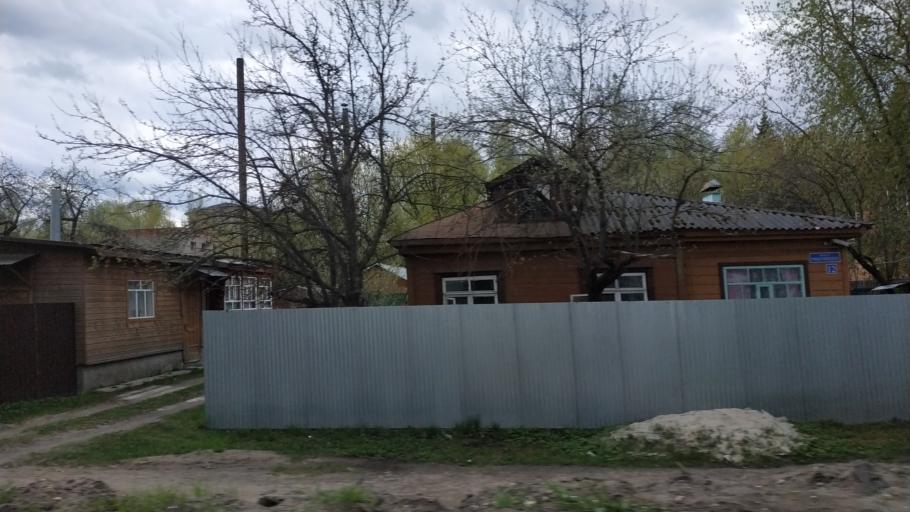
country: RU
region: Moskovskaya
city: Pavlovskiy Posad
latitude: 55.7722
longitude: 38.6888
